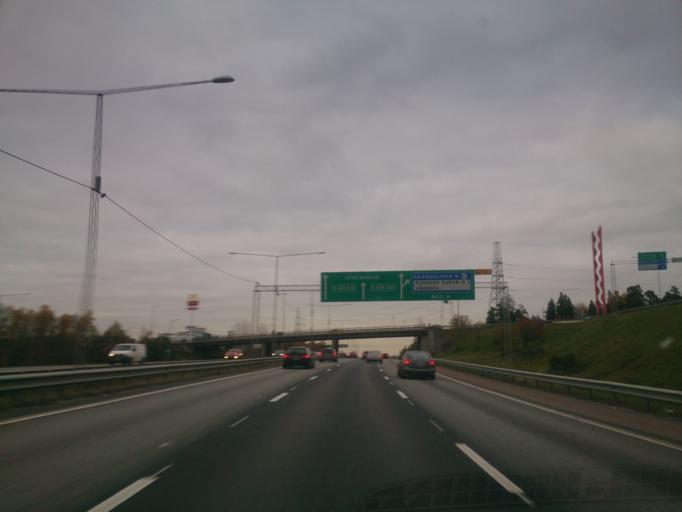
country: SE
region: Stockholm
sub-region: Botkyrka Kommun
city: Fittja
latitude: 59.2631
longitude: 17.8944
